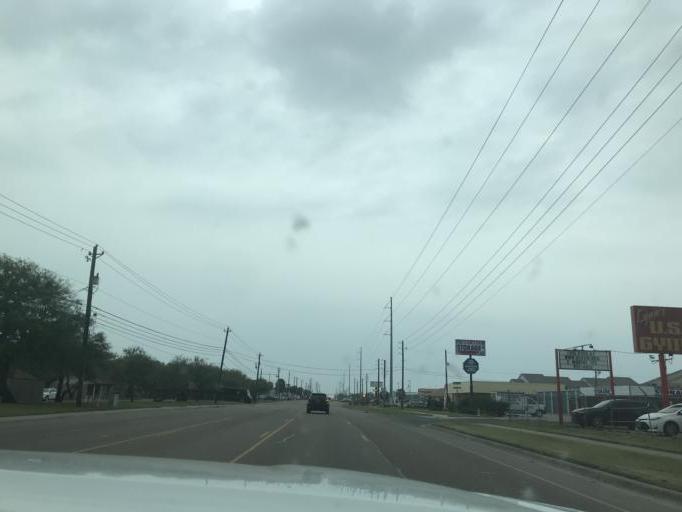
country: US
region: Texas
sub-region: Nueces County
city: Corpus Christi
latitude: 27.6947
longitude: -97.3688
